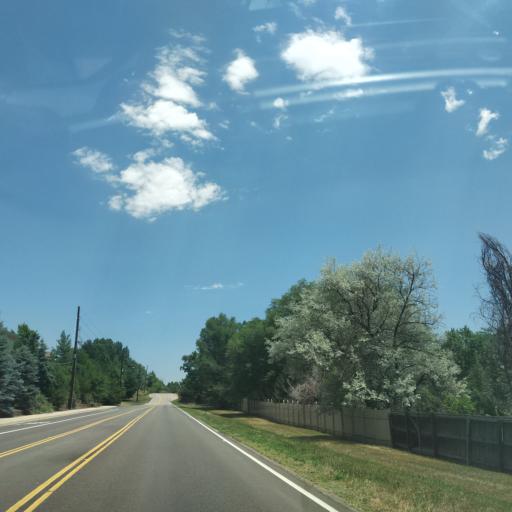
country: US
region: Colorado
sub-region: Jefferson County
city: Lakewood
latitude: 39.6739
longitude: -105.0908
